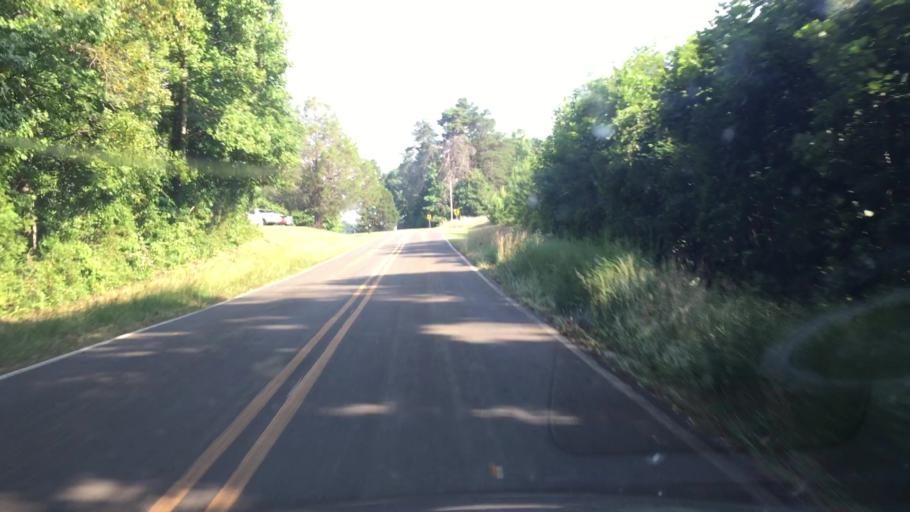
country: US
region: North Carolina
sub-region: Rockingham County
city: Reidsville
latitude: 36.2719
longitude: -79.5662
